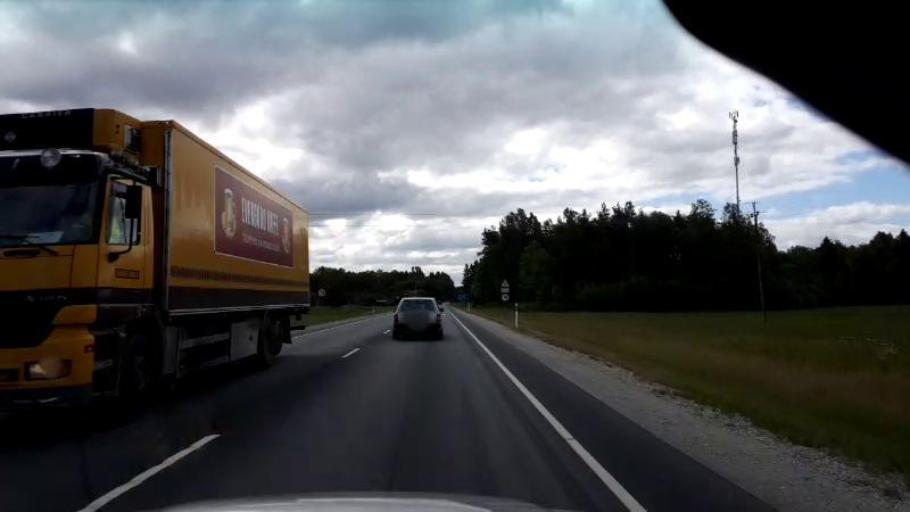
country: EE
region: Paernumaa
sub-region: Halinga vald
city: Parnu-Jaagupi
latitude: 58.6589
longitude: 24.4707
